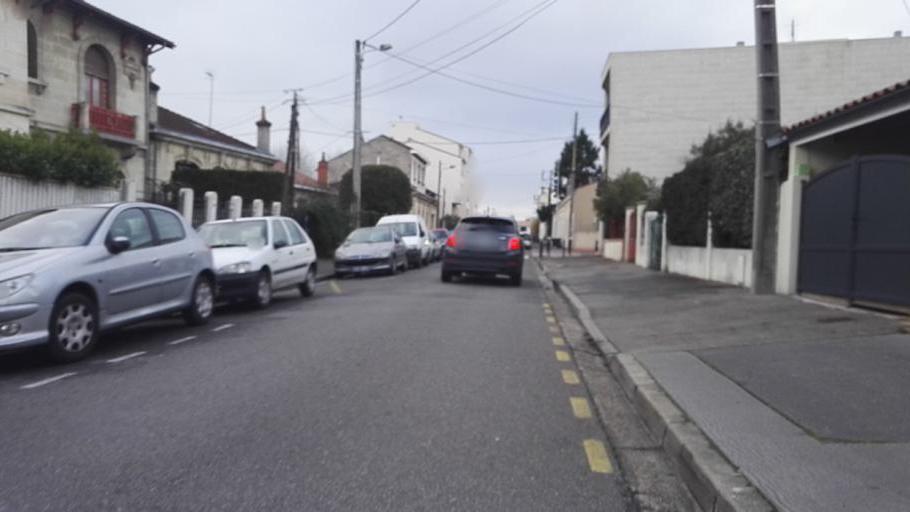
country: FR
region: Aquitaine
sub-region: Departement de la Gironde
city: Le Bouscat
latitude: 44.8470
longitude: -0.6083
